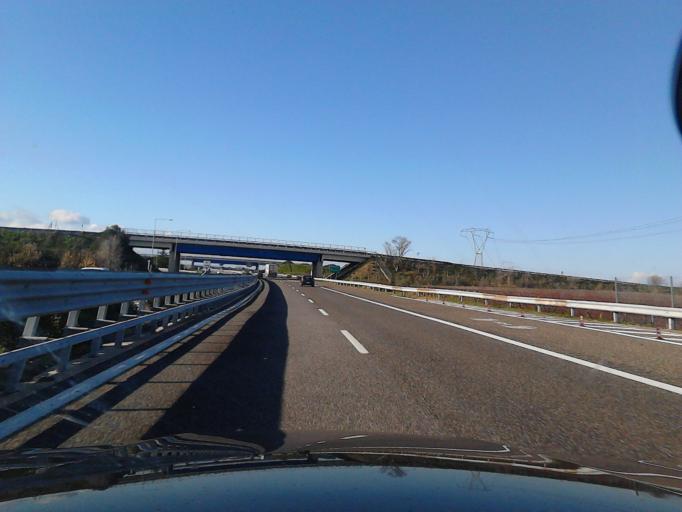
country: IT
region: Apulia
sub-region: Provincia di Foggia
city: Cerignola
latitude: 41.3222
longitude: 15.9022
